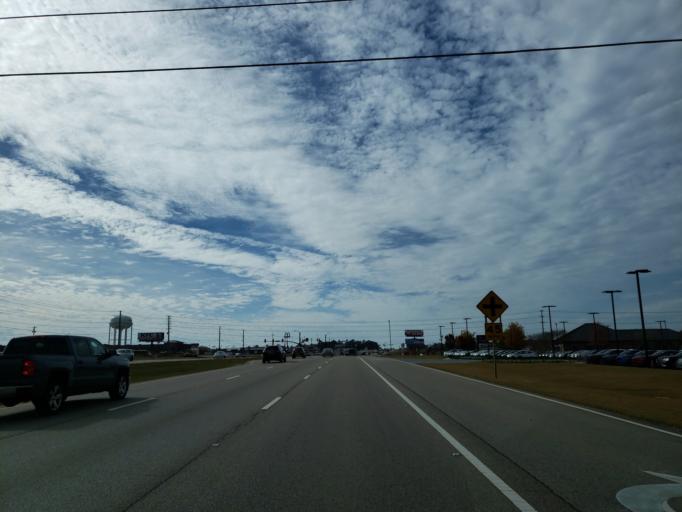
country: US
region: Mississippi
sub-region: Lamar County
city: West Hattiesburg
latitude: 31.3182
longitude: -89.4052
